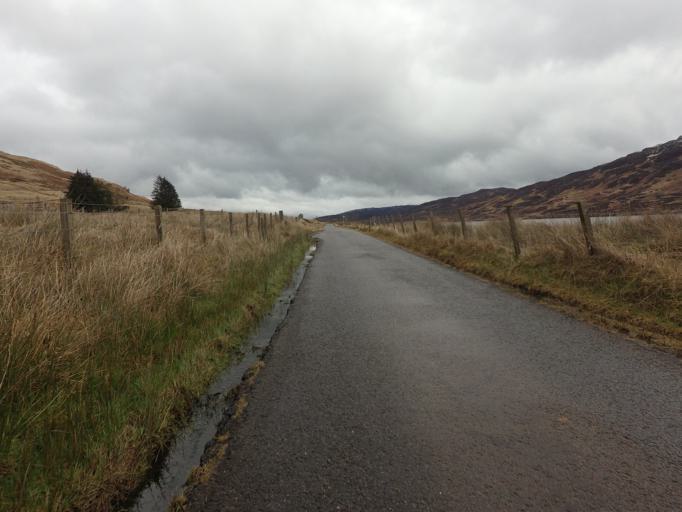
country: GB
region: Scotland
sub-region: West Dunbartonshire
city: Balloch
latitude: 56.2497
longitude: -4.6230
